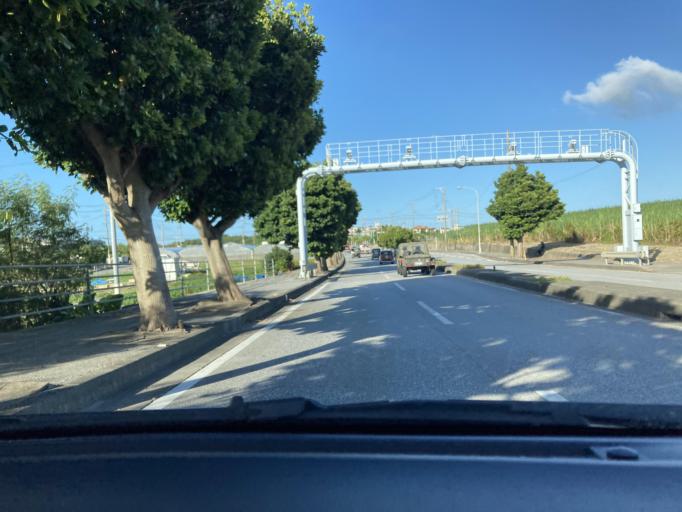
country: JP
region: Okinawa
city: Tomigusuku
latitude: 26.1707
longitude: 127.7094
